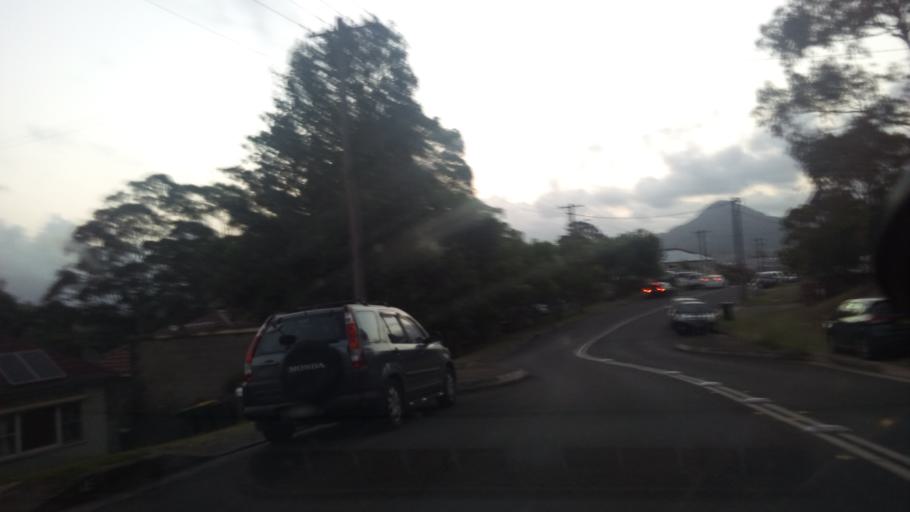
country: AU
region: New South Wales
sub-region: Wollongong
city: Mount Saint Thomas
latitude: -34.4401
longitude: 150.8741
